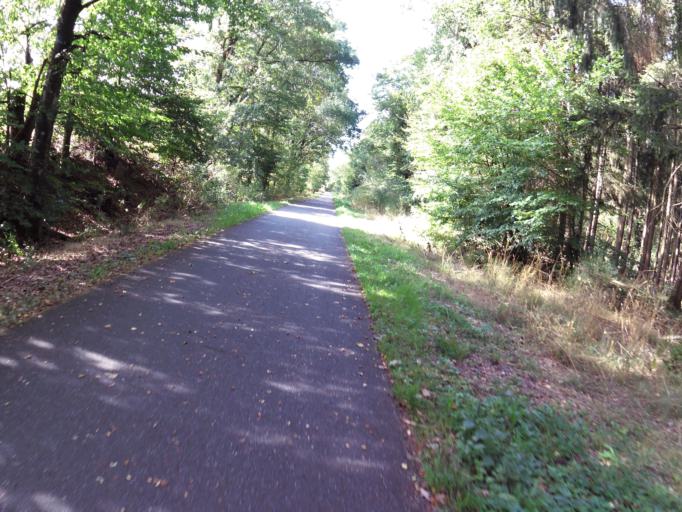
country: DE
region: Rheinland-Pfalz
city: Bleialf
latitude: 50.2164
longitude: 6.2748
